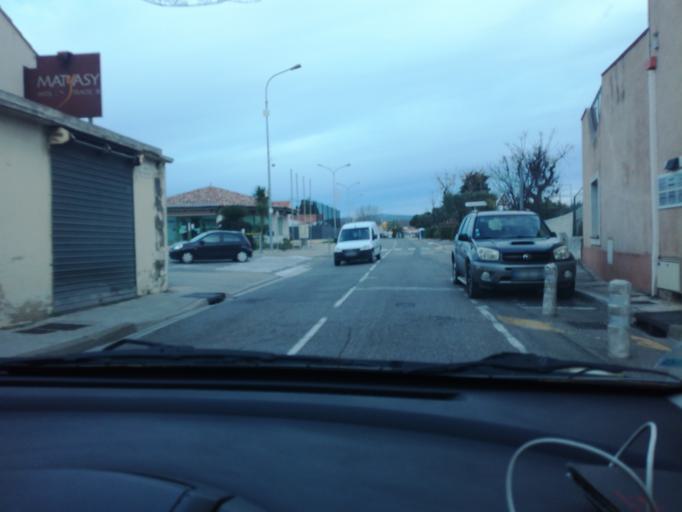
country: FR
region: Provence-Alpes-Cote d'Azur
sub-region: Departement du Var
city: La Crau
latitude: 43.1509
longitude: 6.0732
